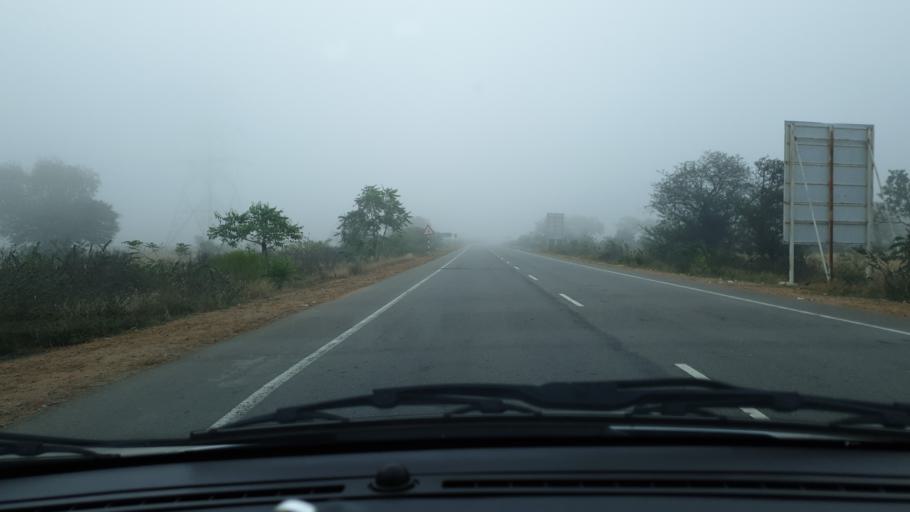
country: IN
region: Telangana
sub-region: Nalgonda
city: Devarkonda
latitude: 16.6096
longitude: 78.6770
